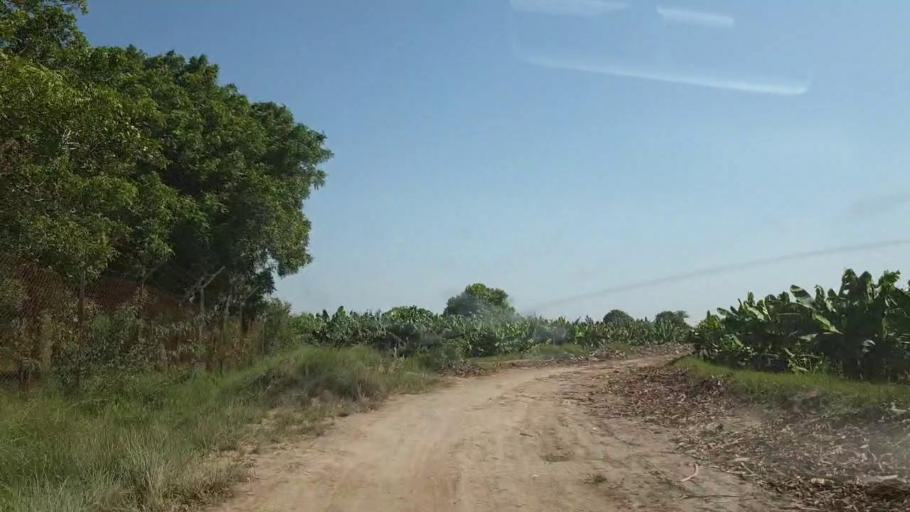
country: PK
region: Sindh
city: Tando Jam
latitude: 25.3727
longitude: 68.5807
